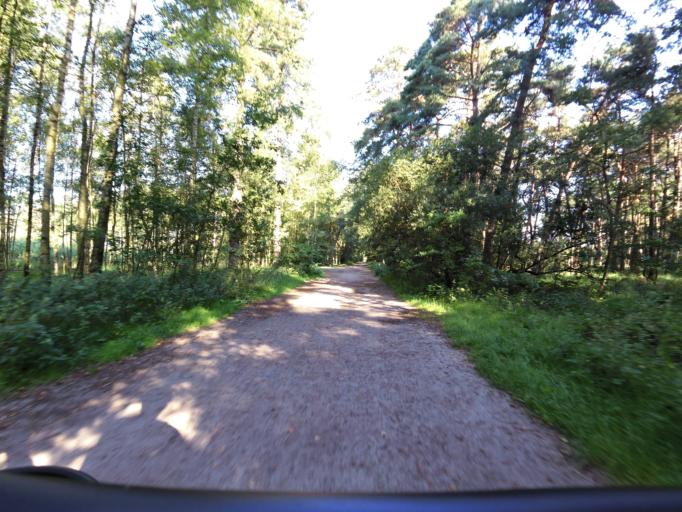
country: BE
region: Flanders
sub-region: Provincie Antwerpen
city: Kalmthout
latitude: 51.3774
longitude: 4.4477
